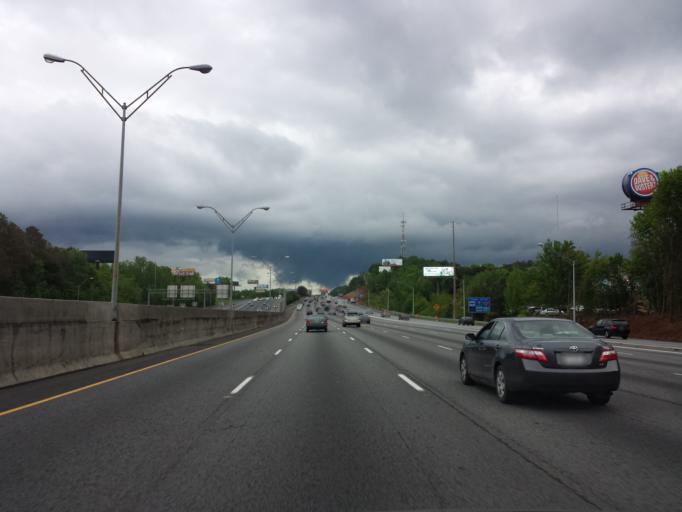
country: US
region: Georgia
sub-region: Cobb County
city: Smyrna
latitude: 33.9213
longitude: -84.4847
